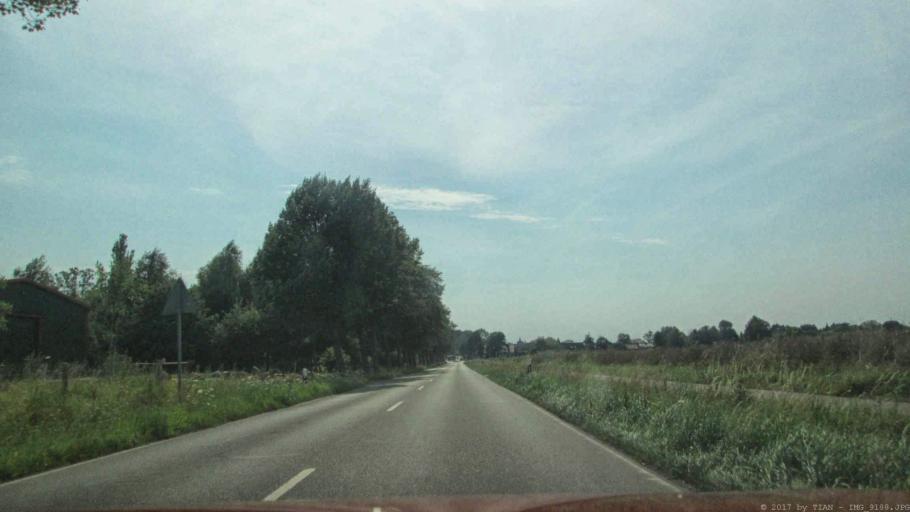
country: DE
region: Lower Saxony
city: Wolfsburg
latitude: 52.4039
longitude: 10.8405
